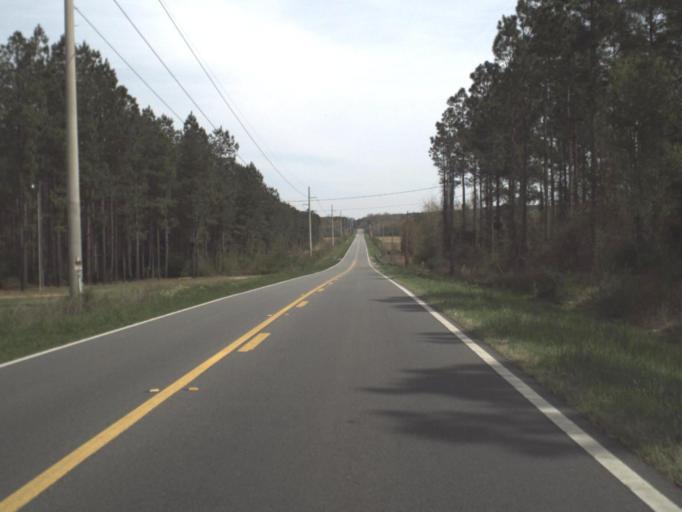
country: US
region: Florida
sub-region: Jackson County
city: Graceville
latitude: 30.9546
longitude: -85.4715
